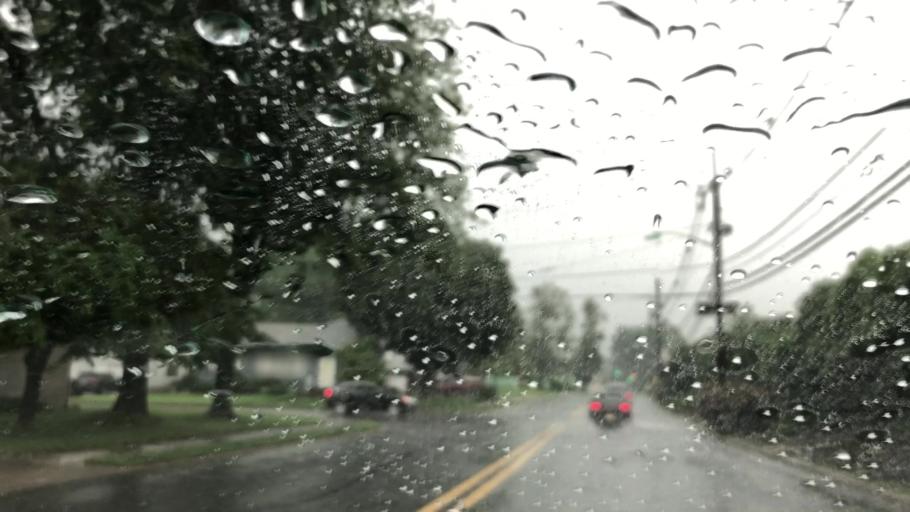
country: US
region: New Jersey
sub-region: Bergen County
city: Saddle Brook
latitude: 40.8997
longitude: -74.1037
